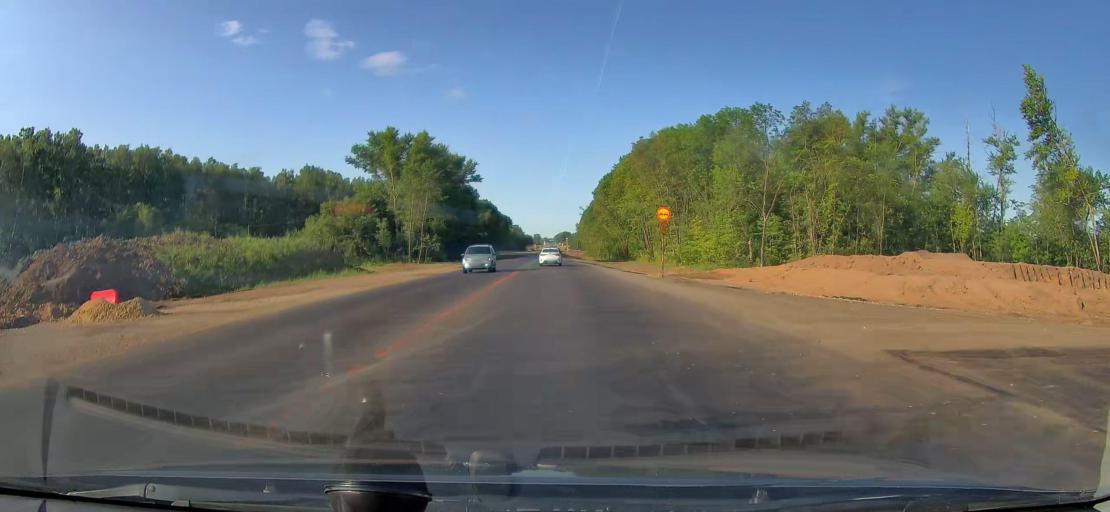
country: RU
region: Orjol
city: Spasskoye-Lutovinovo
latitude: 53.3550
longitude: 36.7187
